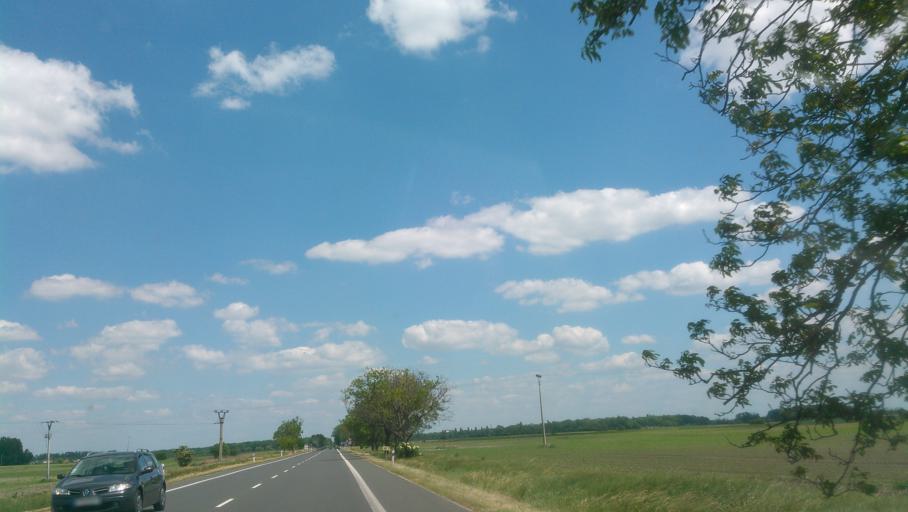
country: SK
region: Trnavsky
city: Dunajska Streda
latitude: 47.9950
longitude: 17.5235
